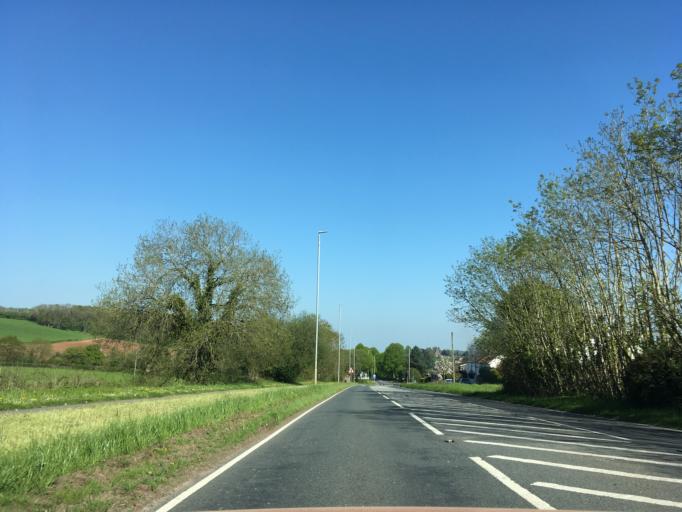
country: GB
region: Wales
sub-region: Newport
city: Llanvaches
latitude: 51.6168
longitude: -2.8485
